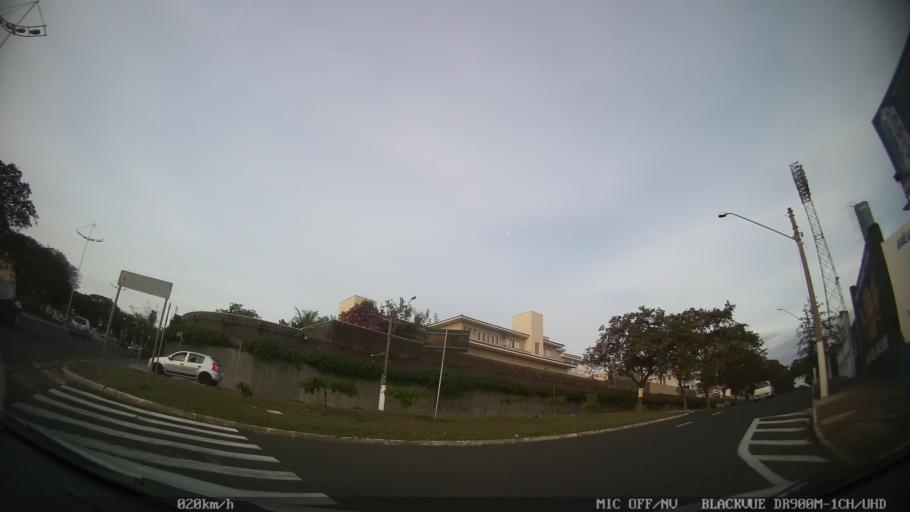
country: BR
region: Sao Paulo
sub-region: Limeira
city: Limeira
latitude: -22.5738
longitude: -47.4127
